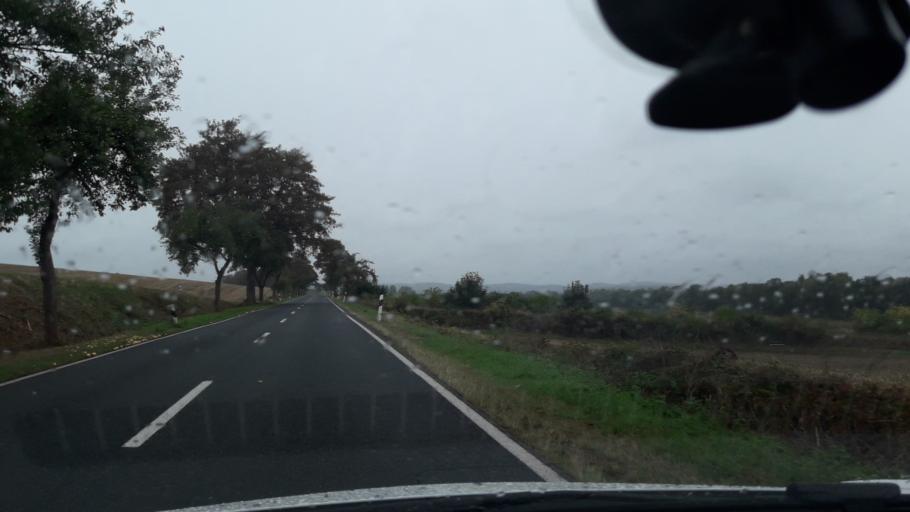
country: DE
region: Lower Saxony
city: Schladen
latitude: 52.0021
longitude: 10.5351
